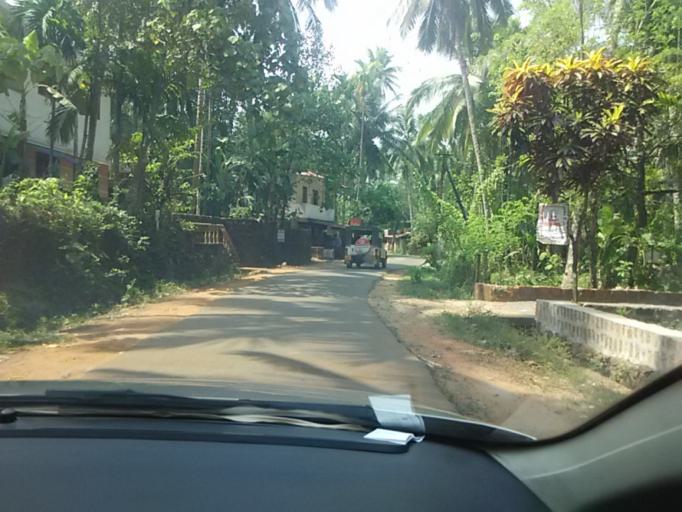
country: IN
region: Kerala
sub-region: Kozhikode
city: Naduvannur
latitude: 11.5419
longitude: 75.7565
